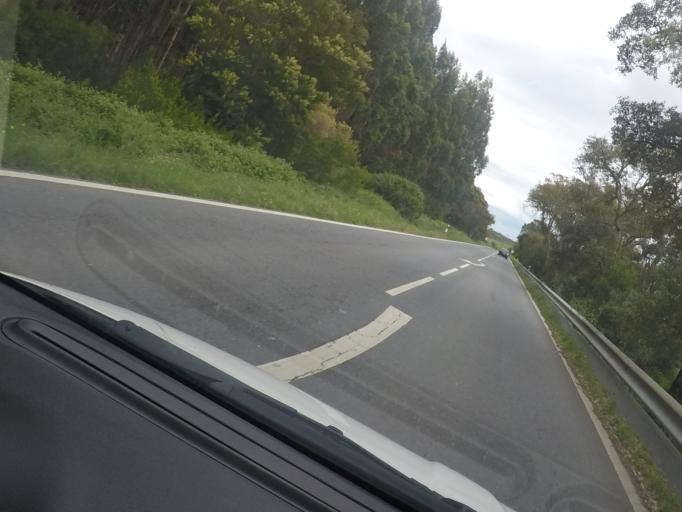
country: PT
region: Setubal
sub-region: Santiago do Cacem
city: Cercal
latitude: 37.7872
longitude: -8.7068
